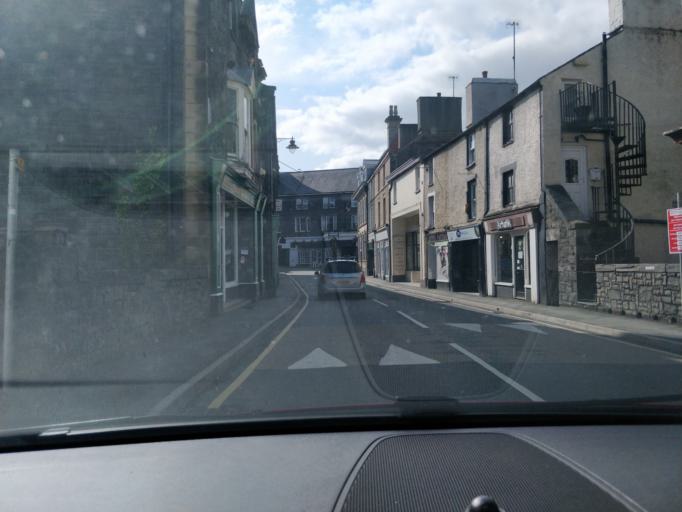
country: GB
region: Wales
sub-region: Conwy
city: Llanrwst
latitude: 53.1391
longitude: -3.7994
